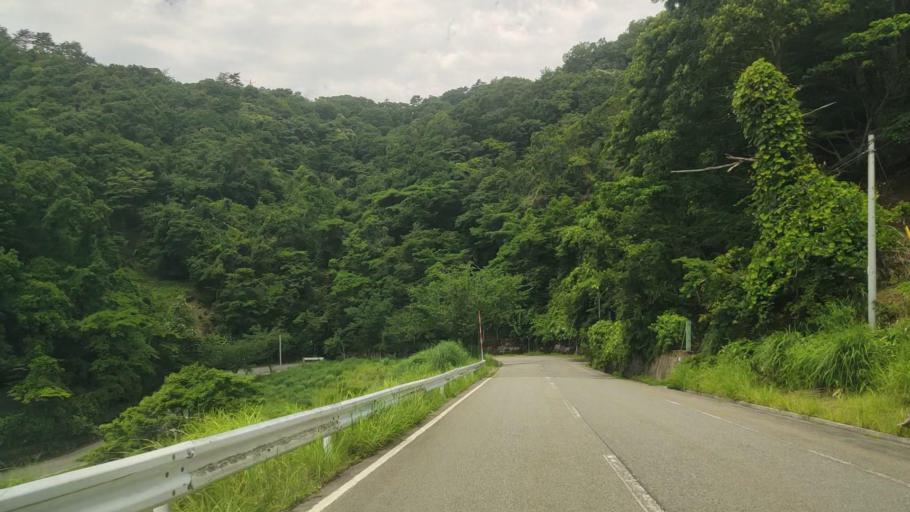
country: JP
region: Hyogo
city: Toyooka
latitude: 35.5172
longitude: 134.6844
